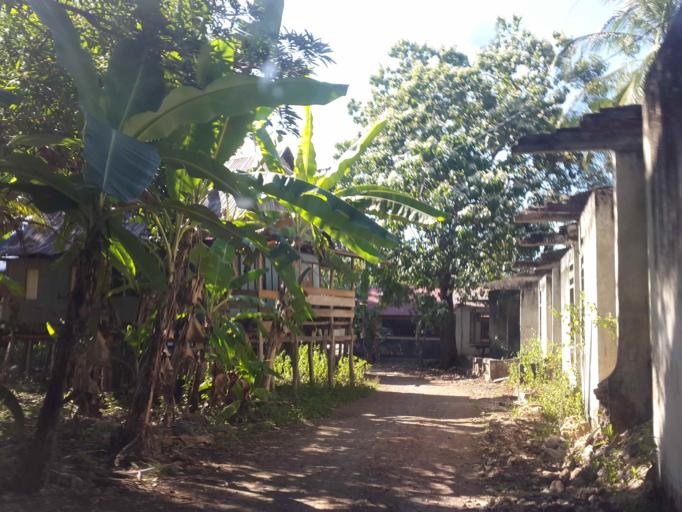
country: ID
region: South Sulawesi
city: Bantaeng
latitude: -5.8609
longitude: 120.5067
